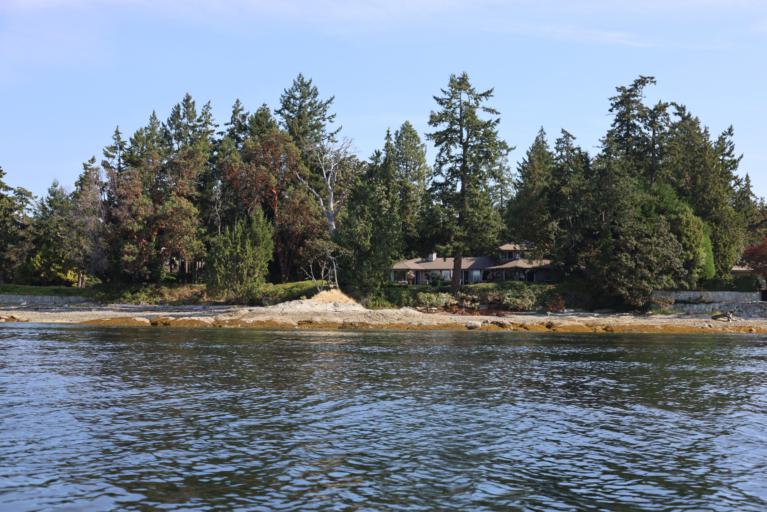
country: CA
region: British Columbia
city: North Saanich
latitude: 48.6638
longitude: -123.4734
